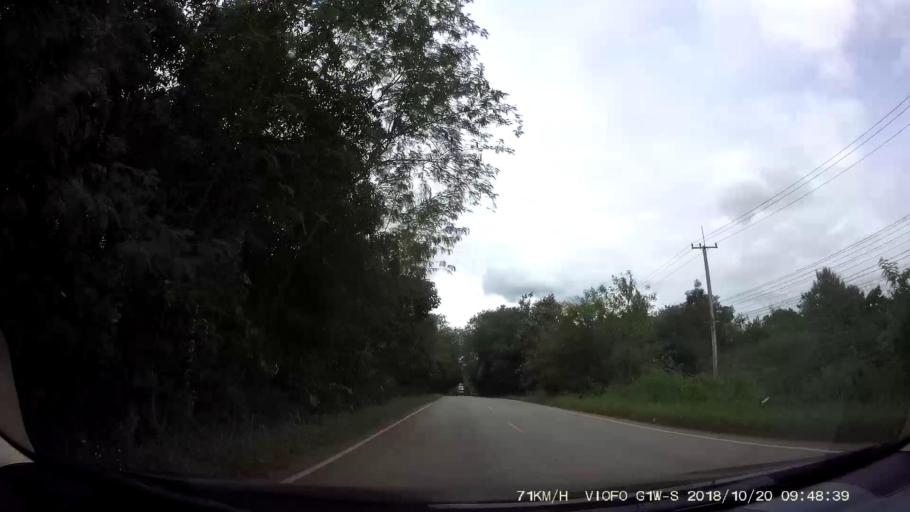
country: TH
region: Chaiyaphum
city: Khon San
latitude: 16.5129
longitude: 101.9104
